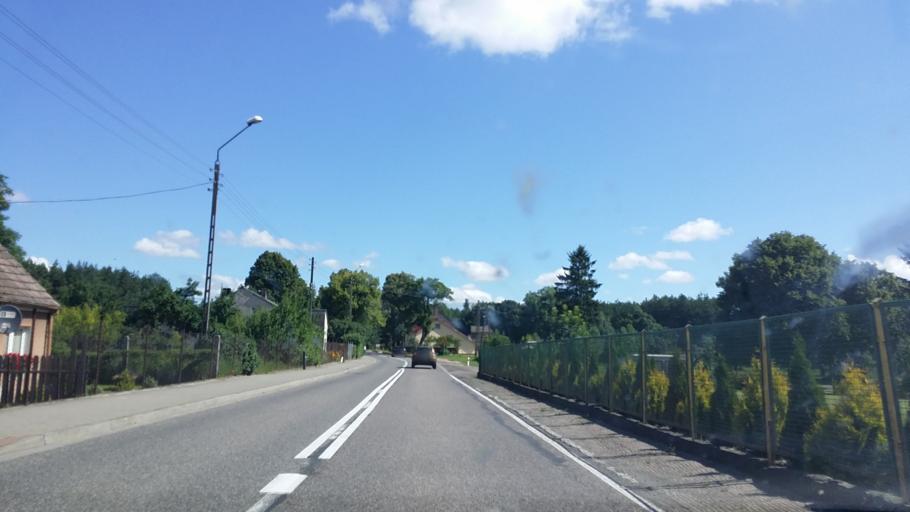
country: PL
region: West Pomeranian Voivodeship
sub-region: Powiat drawski
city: Drawsko Pomorskie
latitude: 53.4427
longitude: 15.8286
